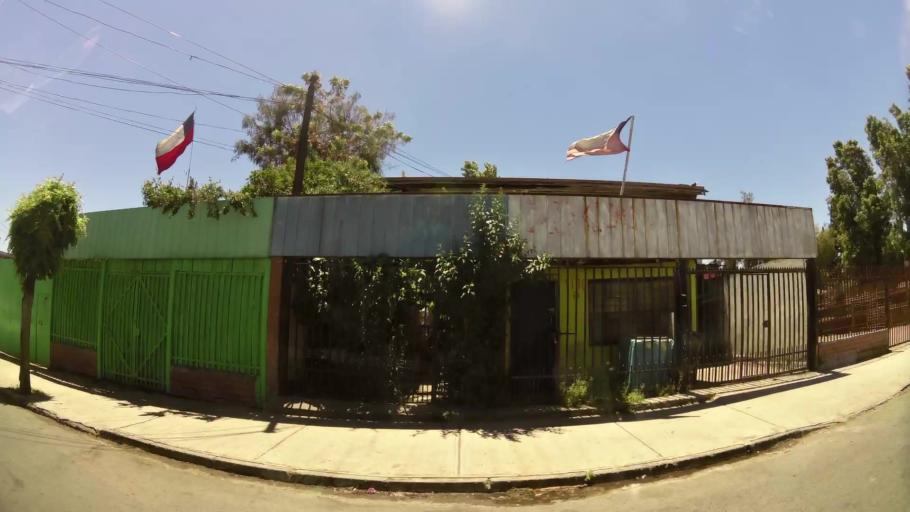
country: CL
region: Santiago Metropolitan
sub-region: Provincia de Maipo
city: San Bernardo
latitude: -33.5804
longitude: -70.6707
